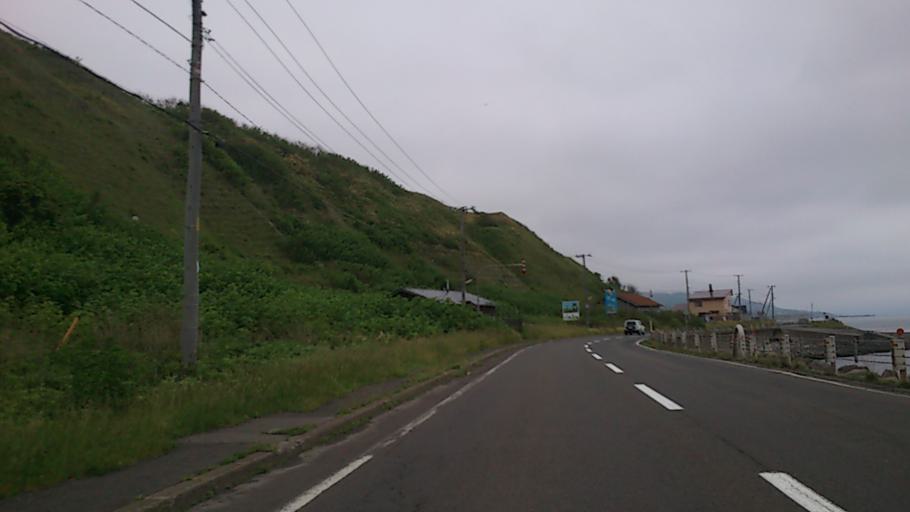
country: JP
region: Hokkaido
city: Iwanai
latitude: 42.8715
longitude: 140.3580
